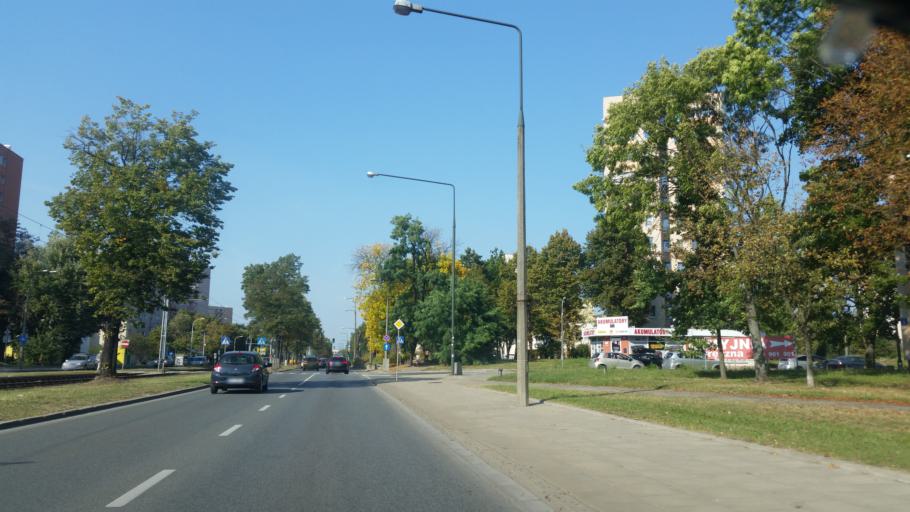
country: PL
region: Masovian Voivodeship
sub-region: Warszawa
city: Bemowo
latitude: 52.2234
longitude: 20.9171
